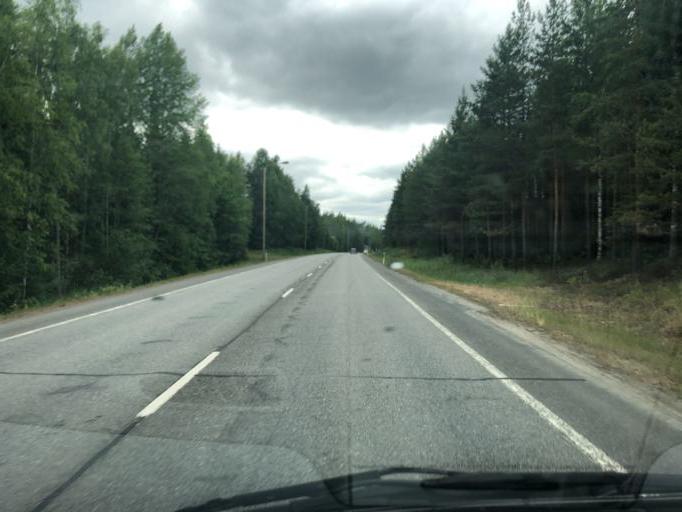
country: FI
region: Kymenlaakso
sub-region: Kouvola
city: Kouvola
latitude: 60.8946
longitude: 26.7543
